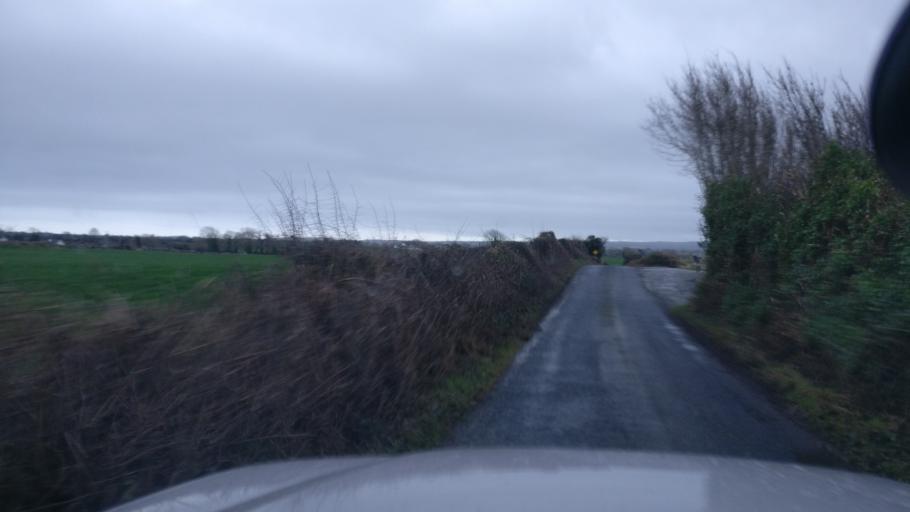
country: IE
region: Connaught
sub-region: County Galway
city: Loughrea
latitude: 53.2050
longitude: -8.6622
